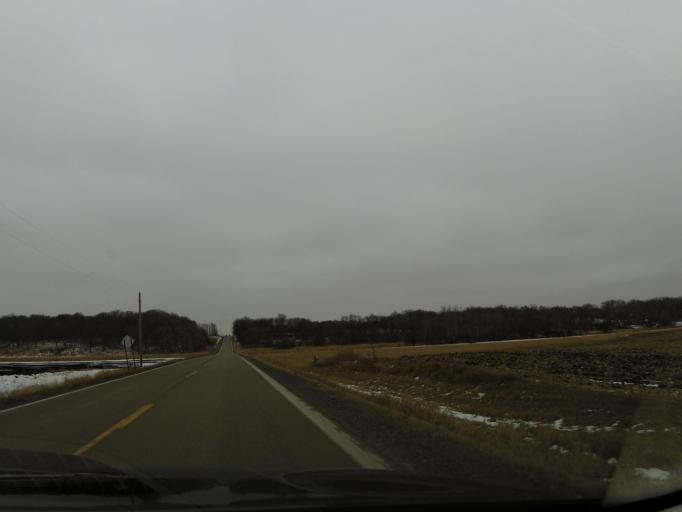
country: US
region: Minnesota
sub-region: Carver County
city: Watertown
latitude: 45.0017
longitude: -93.8488
